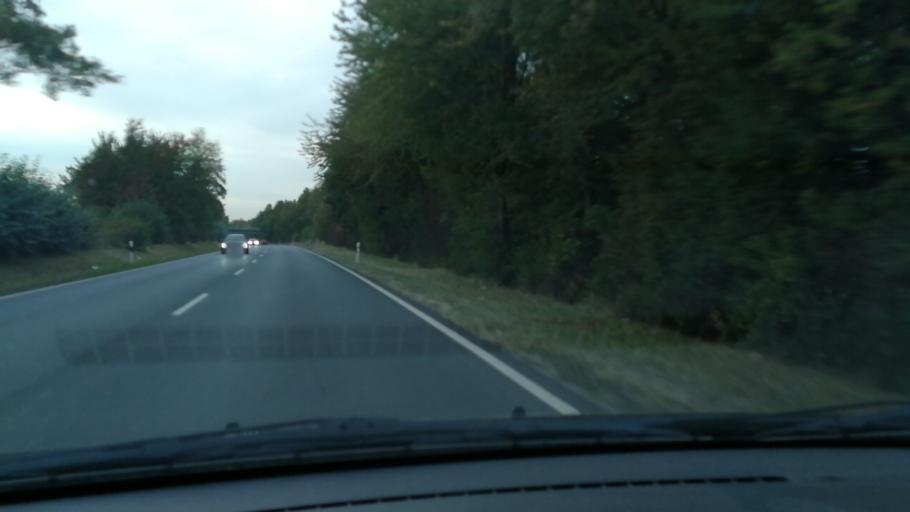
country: DE
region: Hesse
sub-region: Regierungsbezirk Darmstadt
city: Karben
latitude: 50.2221
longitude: 8.7369
